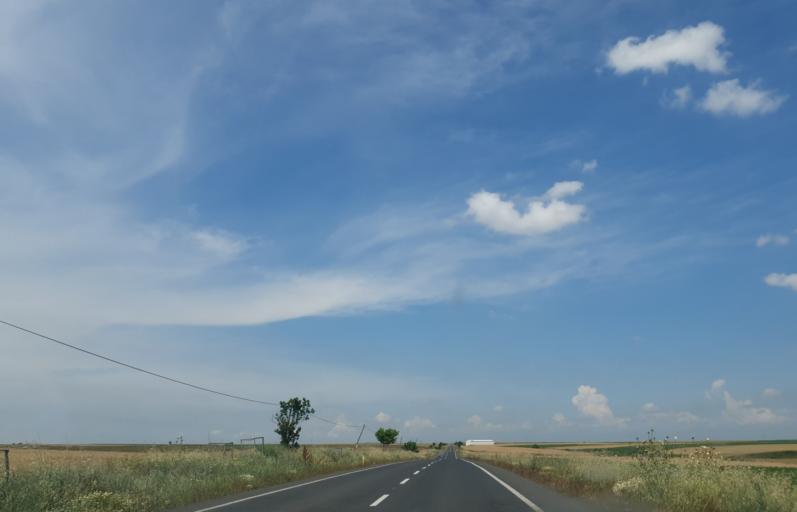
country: TR
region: Kirklareli
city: Buyukkaristiran
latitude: 41.2363
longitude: 27.5893
